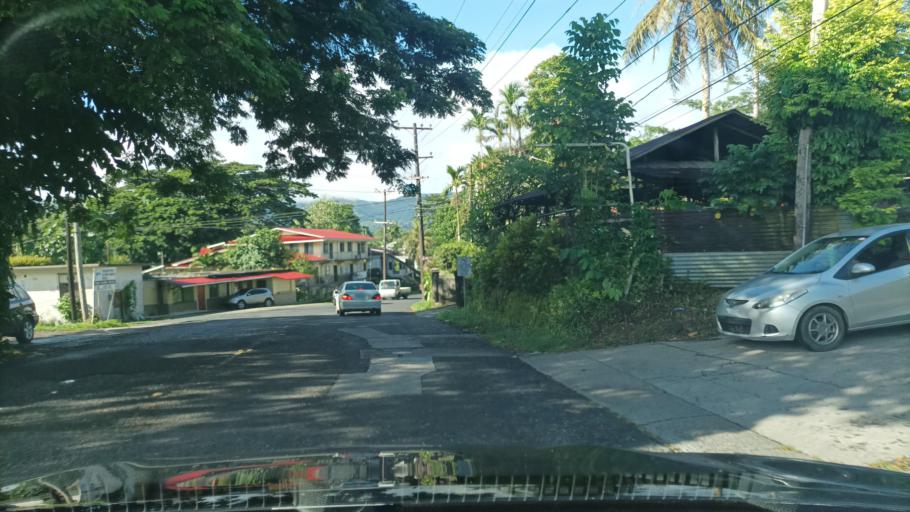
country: FM
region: Pohnpei
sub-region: Kolonia Municipality
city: Kolonia
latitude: 6.9598
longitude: 158.2103
